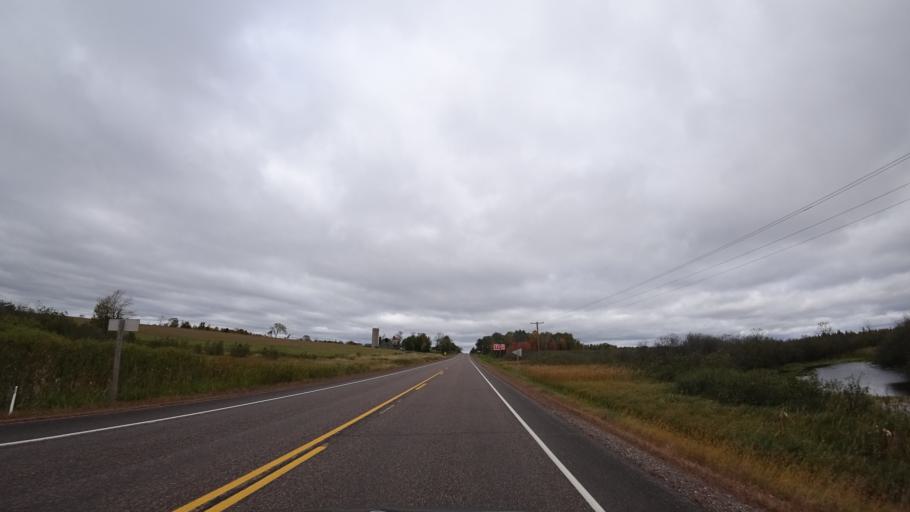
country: US
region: Wisconsin
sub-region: Rusk County
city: Ladysmith
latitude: 45.3653
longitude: -91.1106
